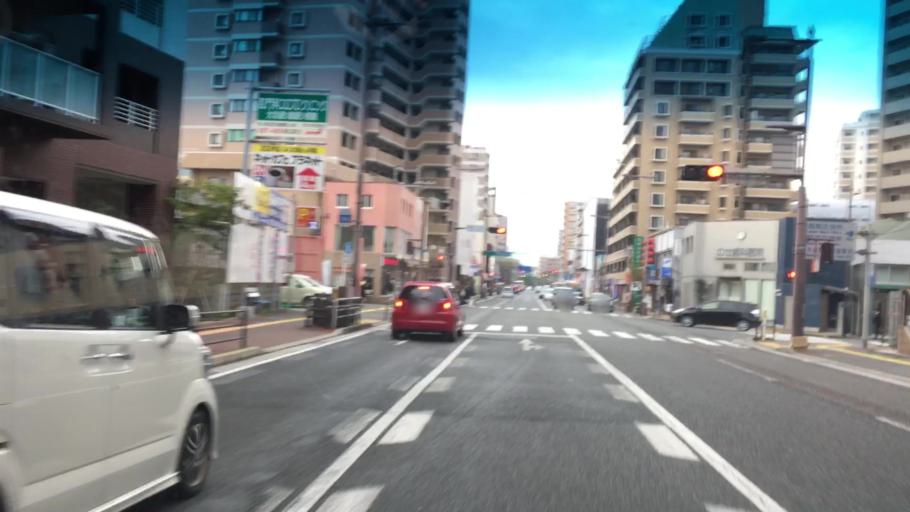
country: JP
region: Fukuoka
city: Fukuoka-shi
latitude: 33.5749
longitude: 130.3713
